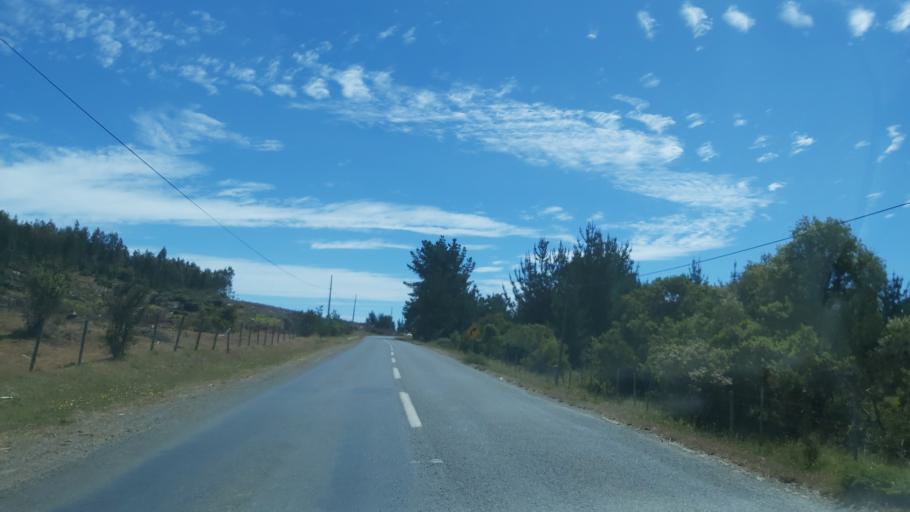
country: CL
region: Maule
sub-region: Provincia de Talca
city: Constitucion
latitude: -35.5388
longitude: -72.5514
